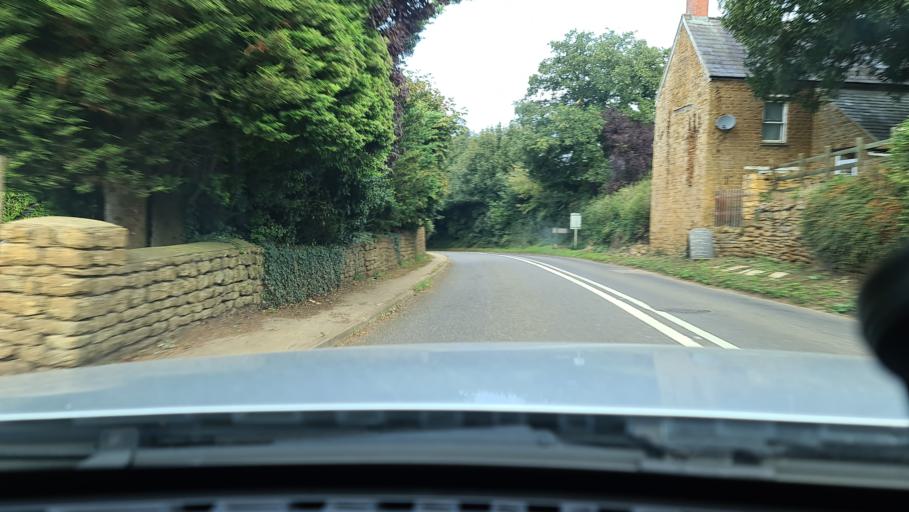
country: GB
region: England
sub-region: Oxfordshire
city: Hanwell
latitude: 52.0741
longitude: -1.3761
